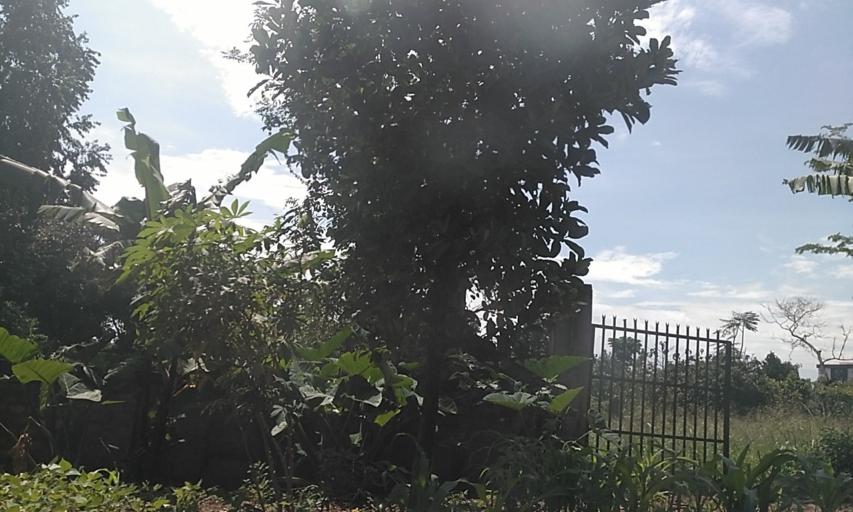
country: UG
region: Central Region
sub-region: Kampala District
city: Kampala
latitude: 0.3260
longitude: 32.6011
